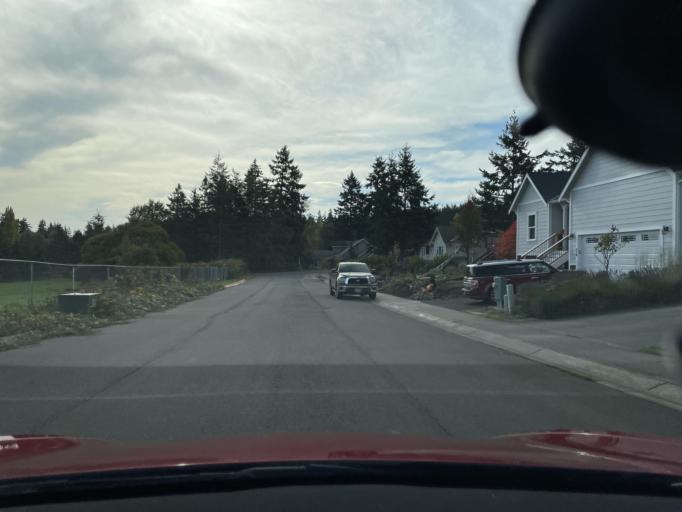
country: US
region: Washington
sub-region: San Juan County
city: Friday Harbor
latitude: 48.5412
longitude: -123.0302
